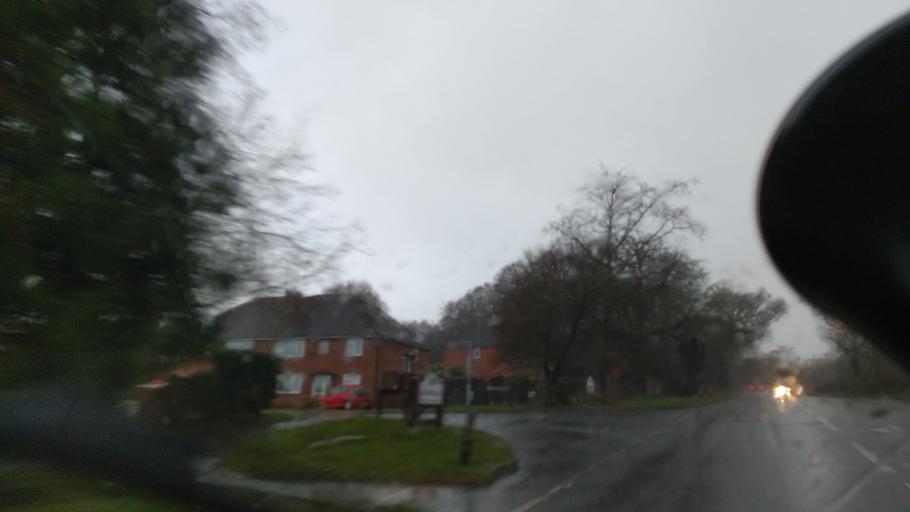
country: GB
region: England
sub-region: West Sussex
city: Arundel
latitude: 50.8546
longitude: -0.5719
